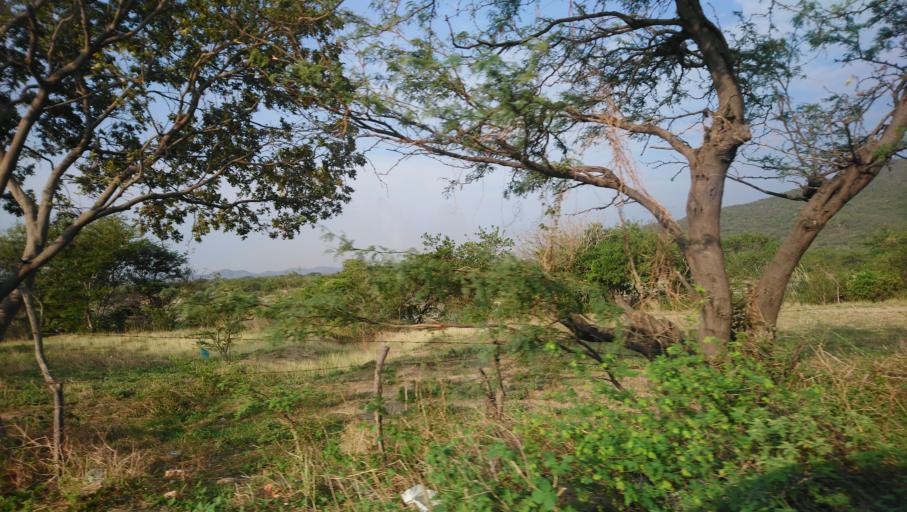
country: MX
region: Oaxaca
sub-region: Salina Cruz
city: Salina Cruz
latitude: 16.2348
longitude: -95.1517
